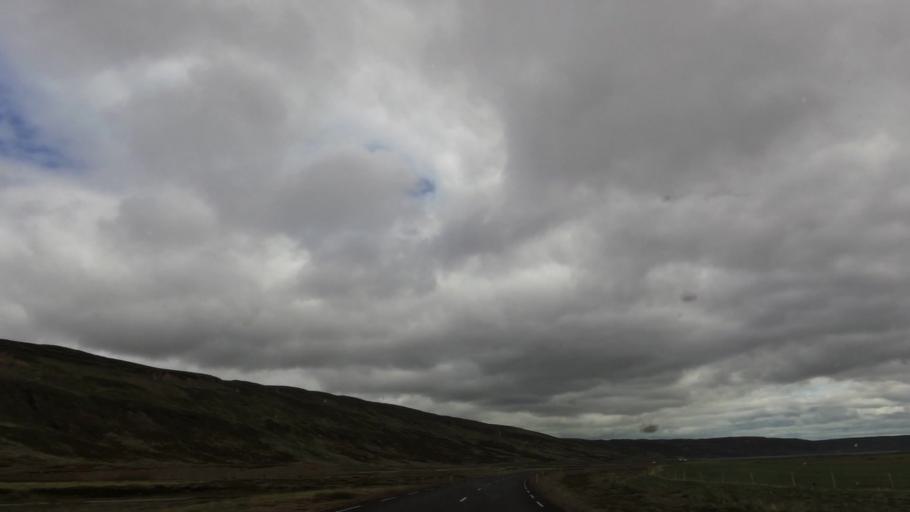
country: IS
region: West
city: Stykkisholmur
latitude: 65.7664
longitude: -21.8301
